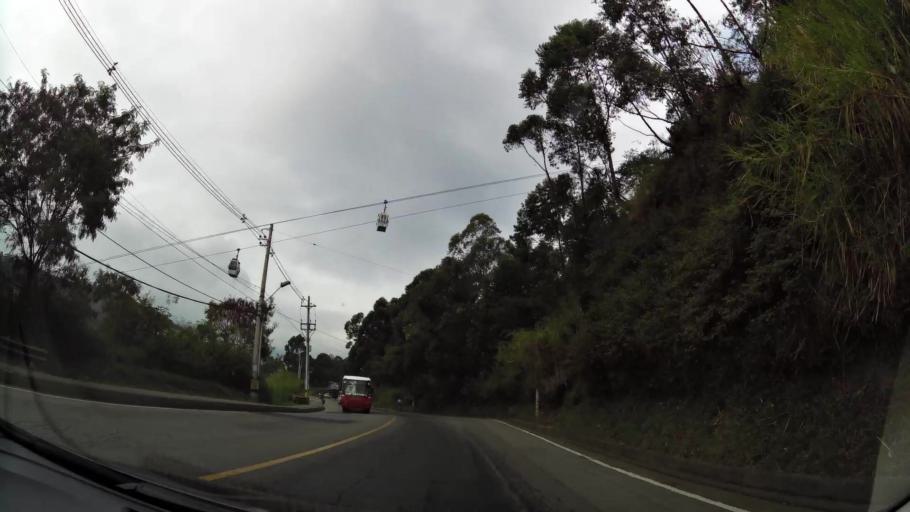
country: CO
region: Antioquia
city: Medellin
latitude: 6.2776
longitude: -75.6137
